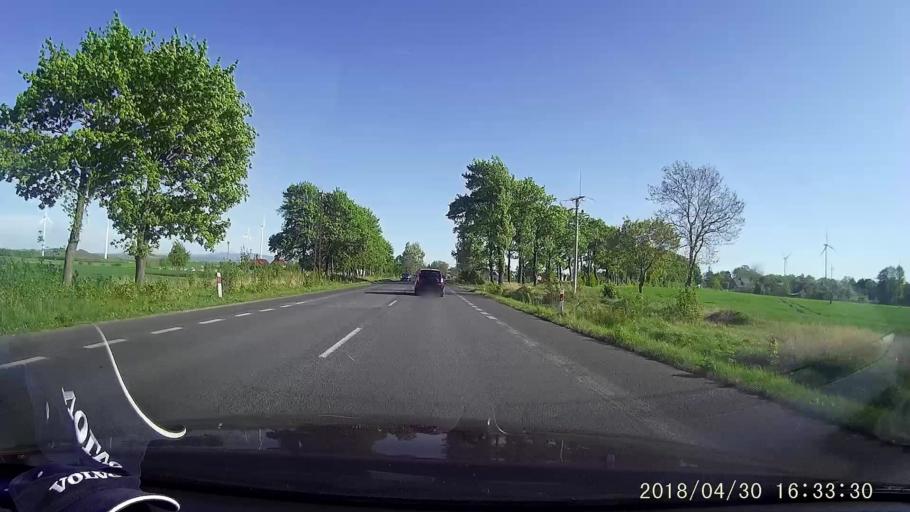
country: PL
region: Lower Silesian Voivodeship
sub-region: Powiat zgorzelecki
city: Sulikow
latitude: 51.0979
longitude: 15.0207
